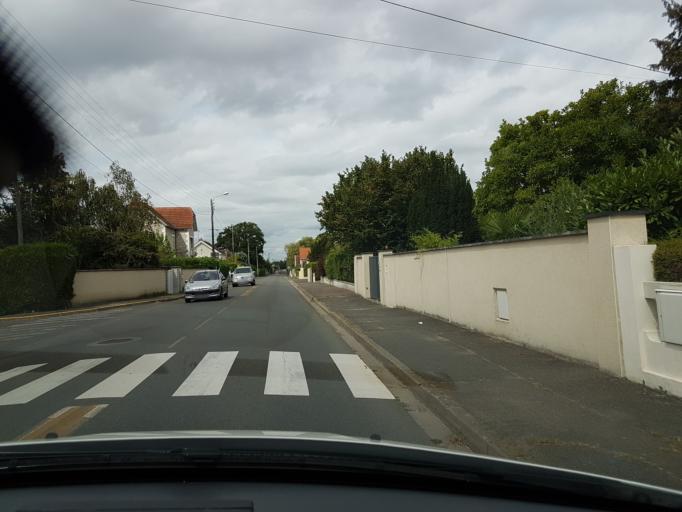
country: FR
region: Centre
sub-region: Departement d'Indre-et-Loire
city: Saint-Avertin
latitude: 47.3498
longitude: 0.7339
